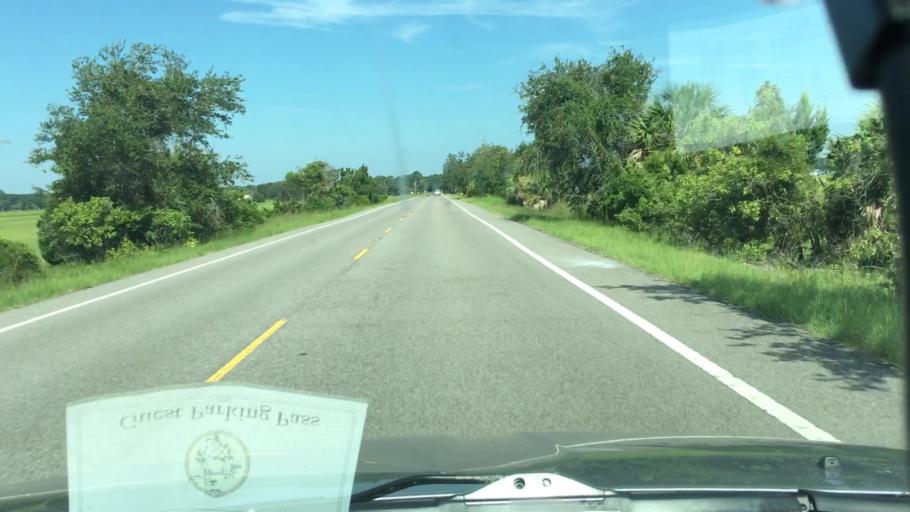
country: US
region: South Carolina
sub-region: Beaufort County
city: Beaufort
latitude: 32.4105
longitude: -80.4708
